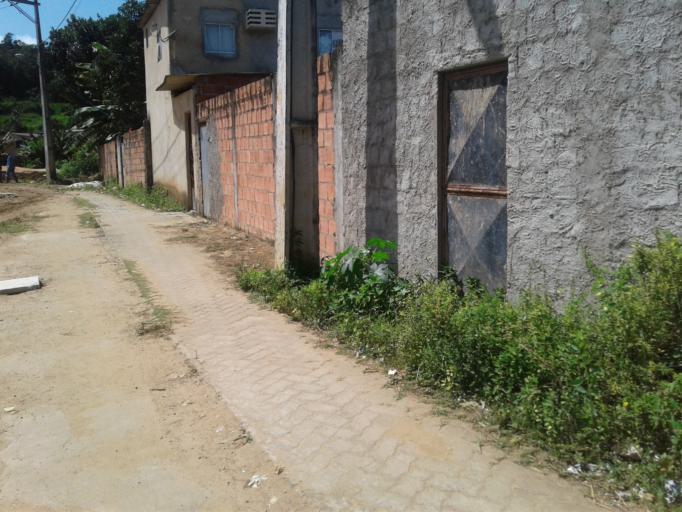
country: BR
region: Bahia
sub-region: Salvador
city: Salvador
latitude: -12.9105
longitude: -38.4717
